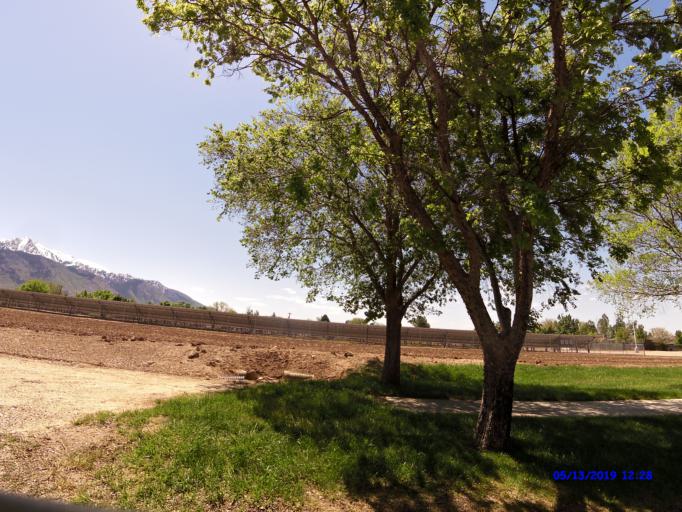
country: US
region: Utah
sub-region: Weber County
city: Harrisville
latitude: 41.2623
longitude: -111.9613
